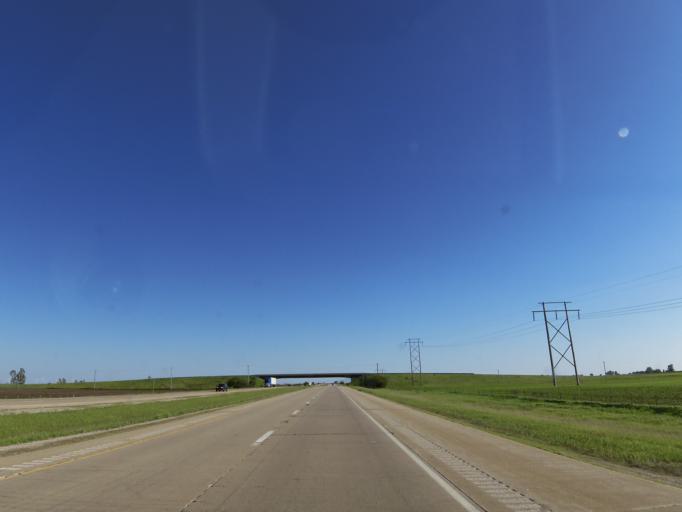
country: US
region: Illinois
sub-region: Woodford County
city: Minonk
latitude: 40.9579
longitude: -89.0567
